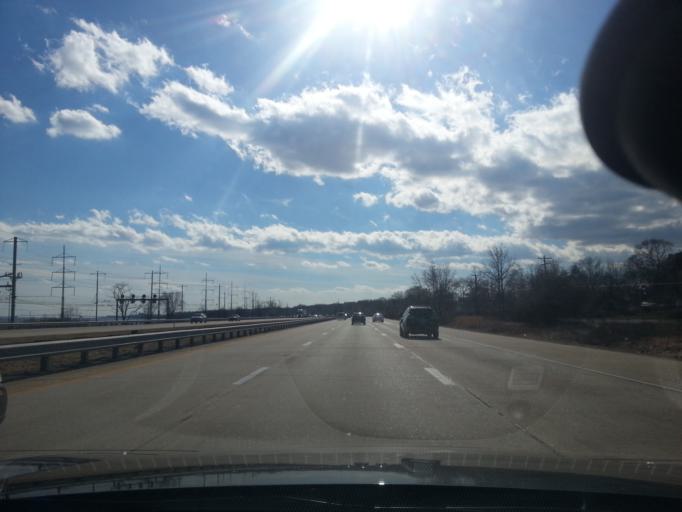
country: US
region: Delaware
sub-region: New Castle County
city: Claymont
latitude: 39.7917
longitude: -75.4630
